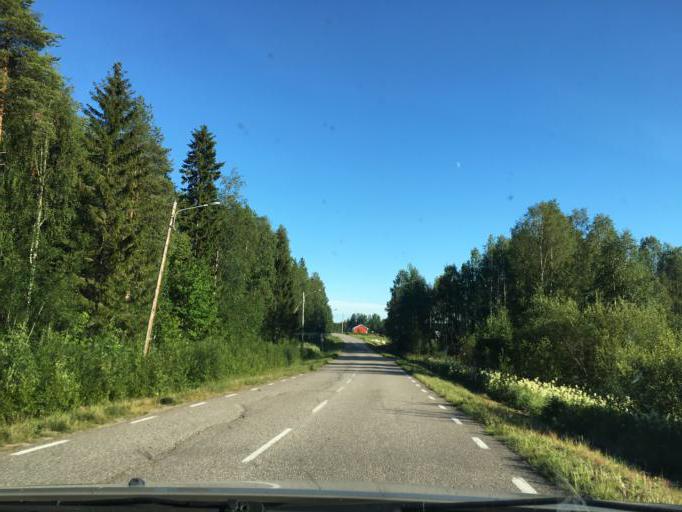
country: SE
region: Norrbotten
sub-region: Kalix Kommun
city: Rolfs
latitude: 65.9043
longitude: 22.9302
